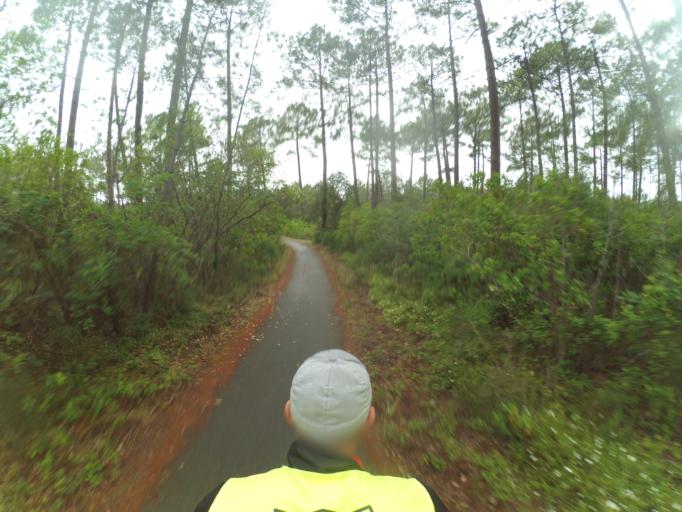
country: FR
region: Aquitaine
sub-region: Departement des Landes
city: Mimizan
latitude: 44.2217
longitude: -1.2524
